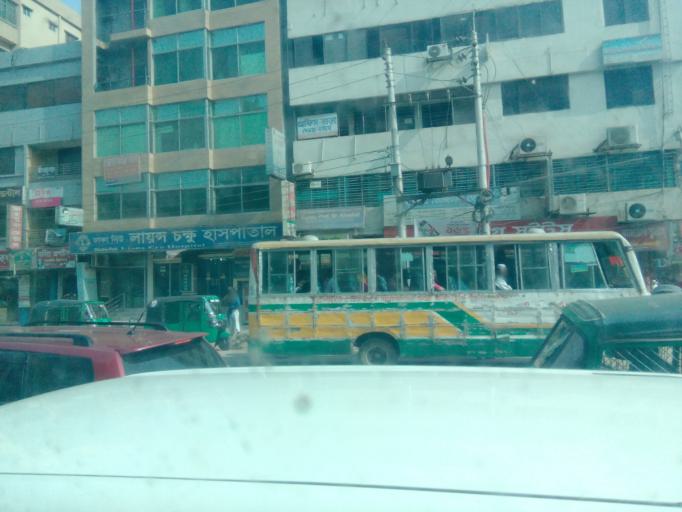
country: BD
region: Dhaka
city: Paltan
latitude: 23.7770
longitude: 90.4257
